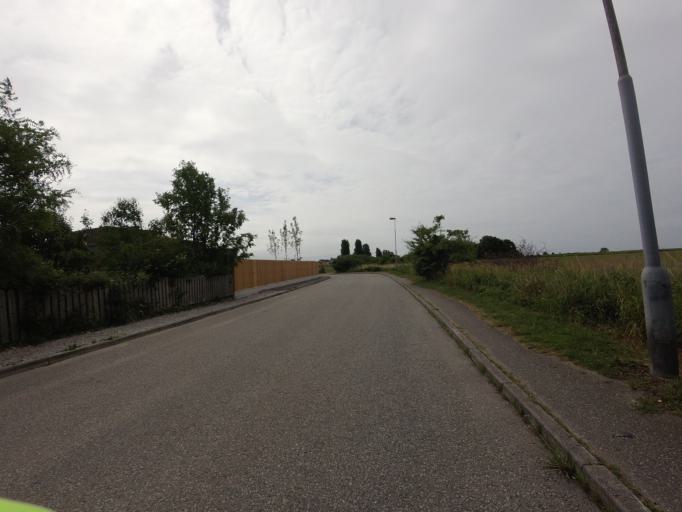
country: SE
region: Skane
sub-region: Malmo
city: Bunkeflostrand
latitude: 55.5589
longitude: 12.9080
